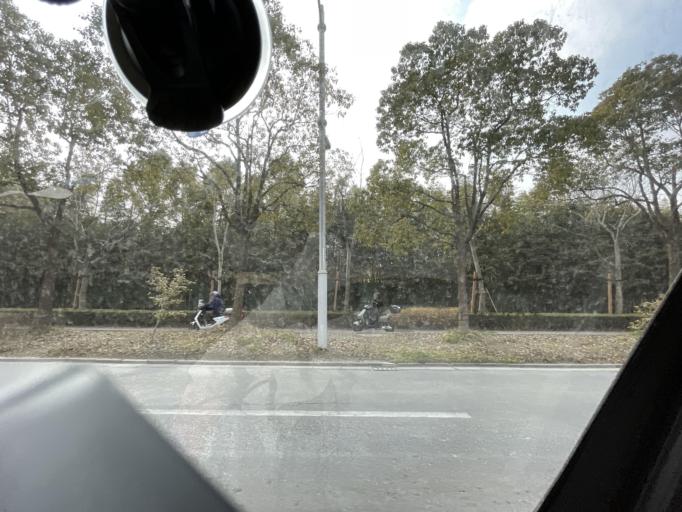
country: CN
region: Shanghai Shi
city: Yangpu
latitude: 31.3220
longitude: 121.5062
